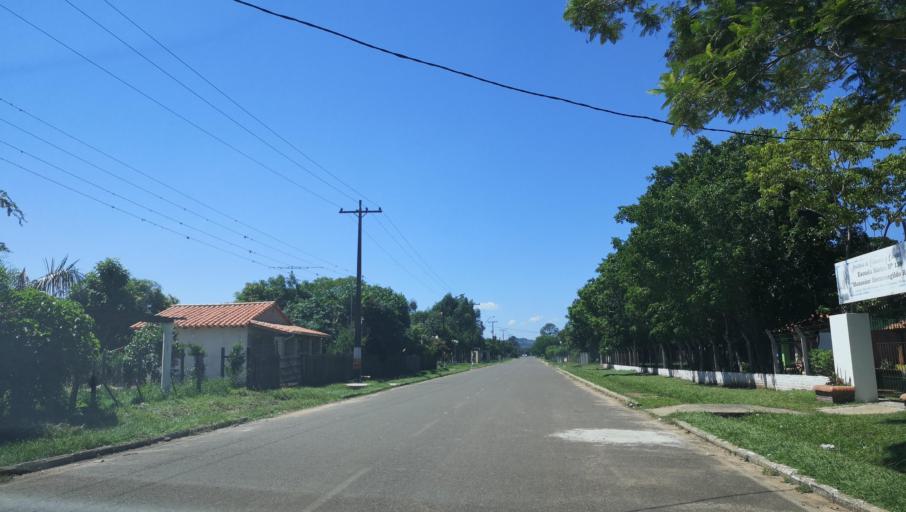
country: PY
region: Caaguazu
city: Carayao
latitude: -25.1966
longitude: -56.4032
